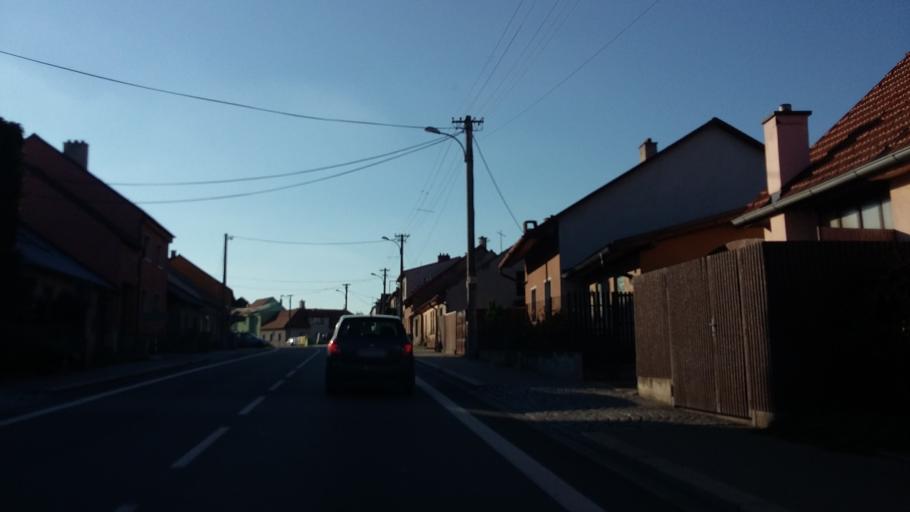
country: CZ
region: Vysocina
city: Merin
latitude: 49.3946
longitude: 15.8809
